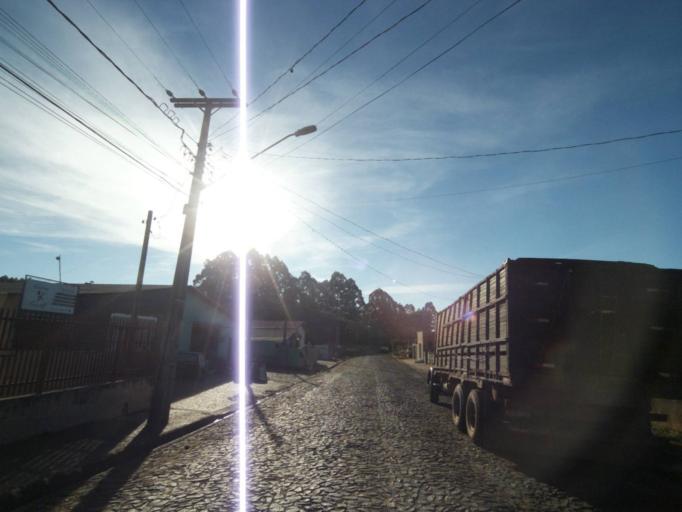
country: BR
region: Parana
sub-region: Tibagi
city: Tibagi
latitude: -24.5084
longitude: -50.4158
